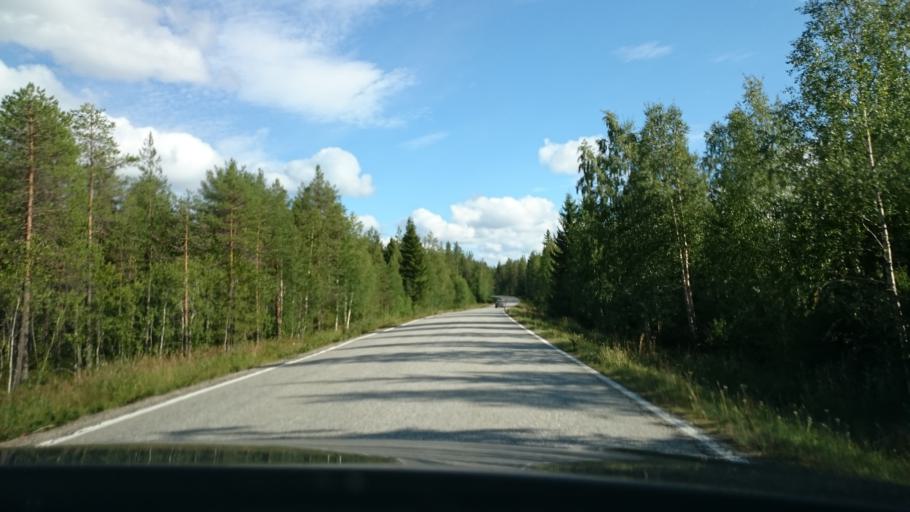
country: FI
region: Kainuu
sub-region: Kehys-Kainuu
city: Suomussalmi
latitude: 64.7545
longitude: 29.4150
